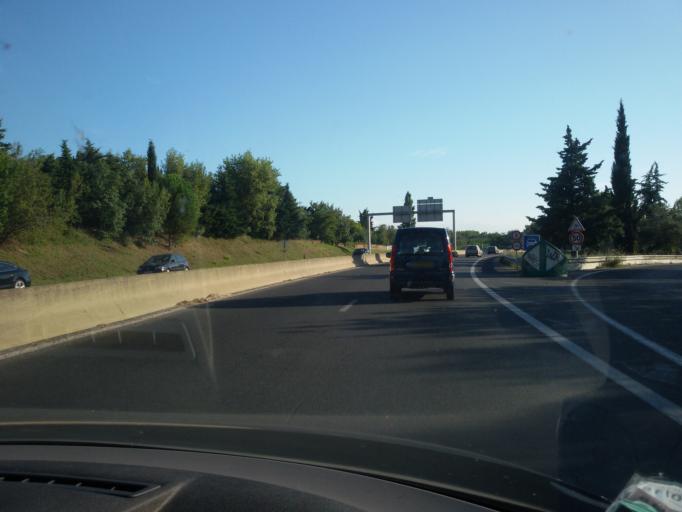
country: FR
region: Languedoc-Roussillon
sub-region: Departement de l'Herault
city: Juvignac
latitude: 43.6096
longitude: 3.8221
